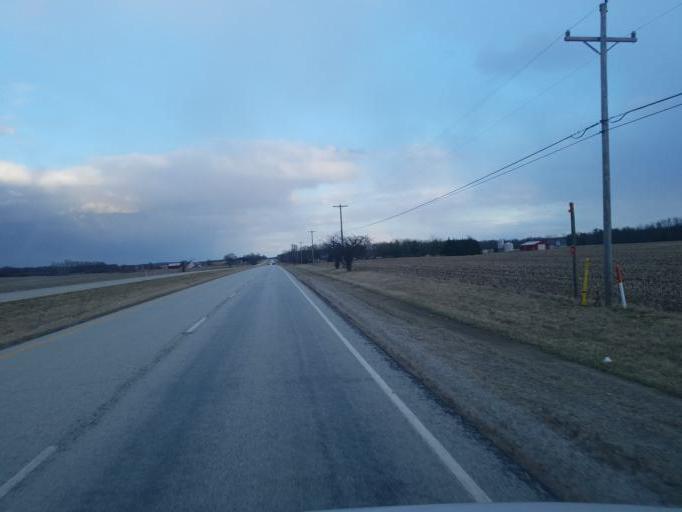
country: US
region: Indiana
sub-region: Henry County
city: Knightstown
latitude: 39.7925
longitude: -85.5778
